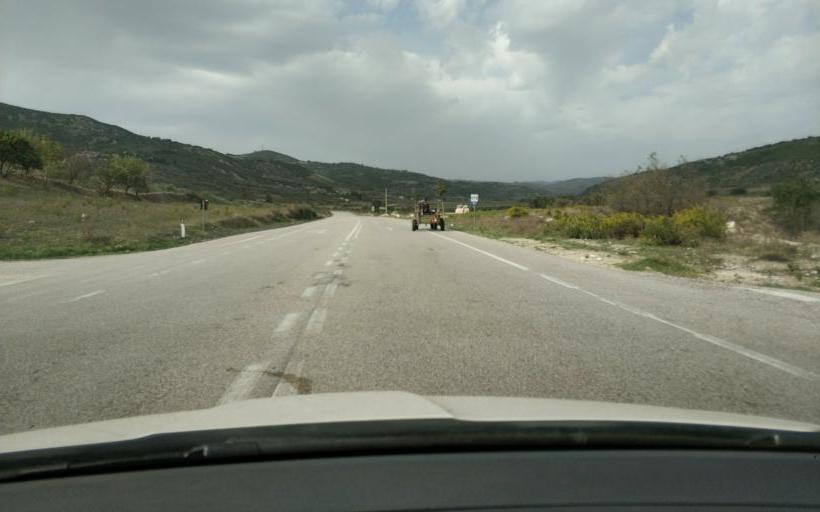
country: AL
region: Gjirokaster
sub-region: Rrethi i Tepelenes
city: Krahes
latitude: 40.4346
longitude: 19.8515
